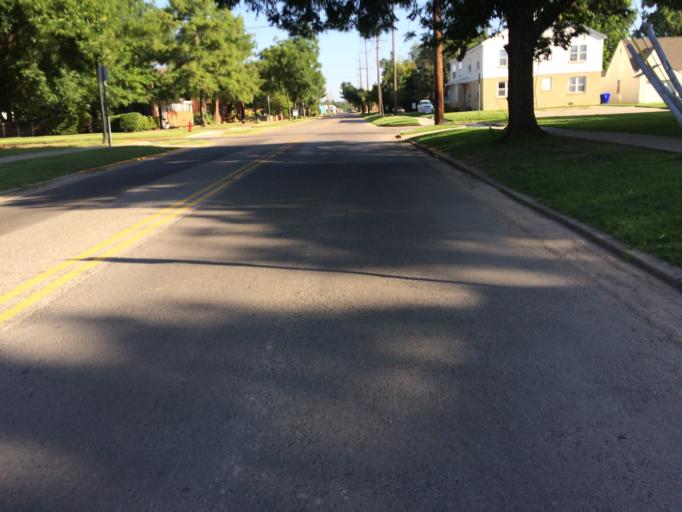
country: US
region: Oklahoma
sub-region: Cleveland County
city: Norman
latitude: 35.2164
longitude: -97.4447
